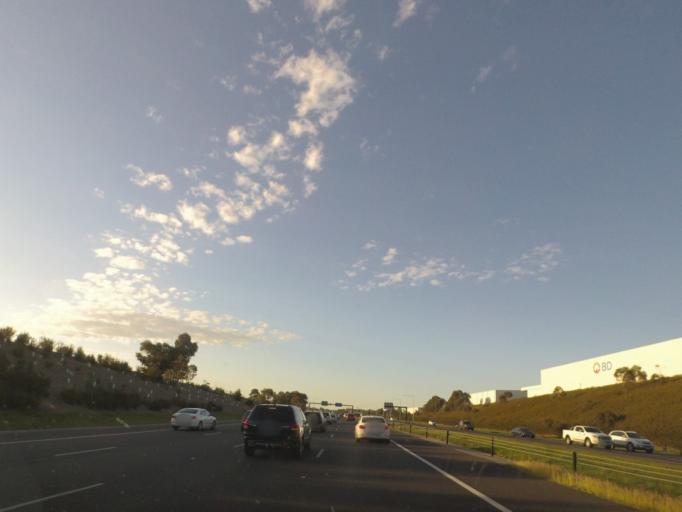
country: AU
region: Victoria
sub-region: Monash
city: Mulgrave
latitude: -37.9107
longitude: 145.2159
